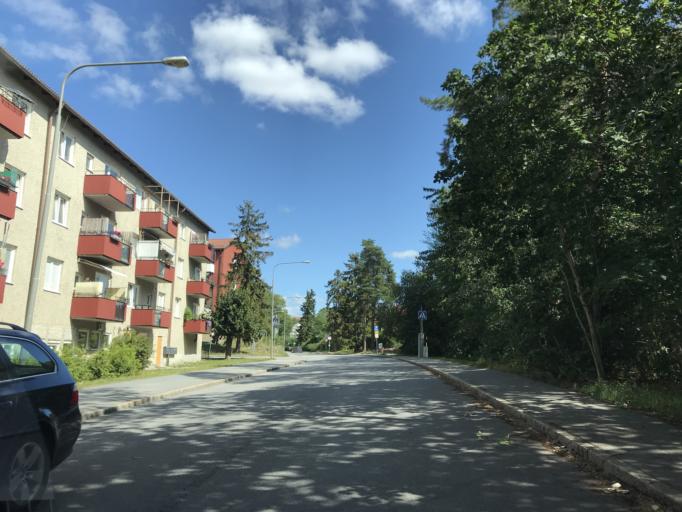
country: SE
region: Stockholm
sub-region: Huddinge Kommun
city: Segeltorp
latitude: 59.2908
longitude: 17.9737
